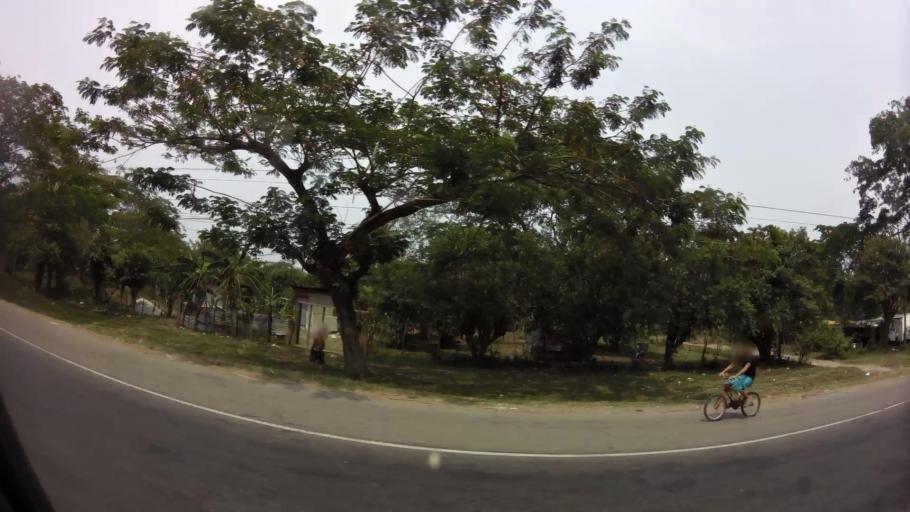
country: HN
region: Cortes
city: Nuevo Chamelecon
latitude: 15.3805
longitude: -87.9894
